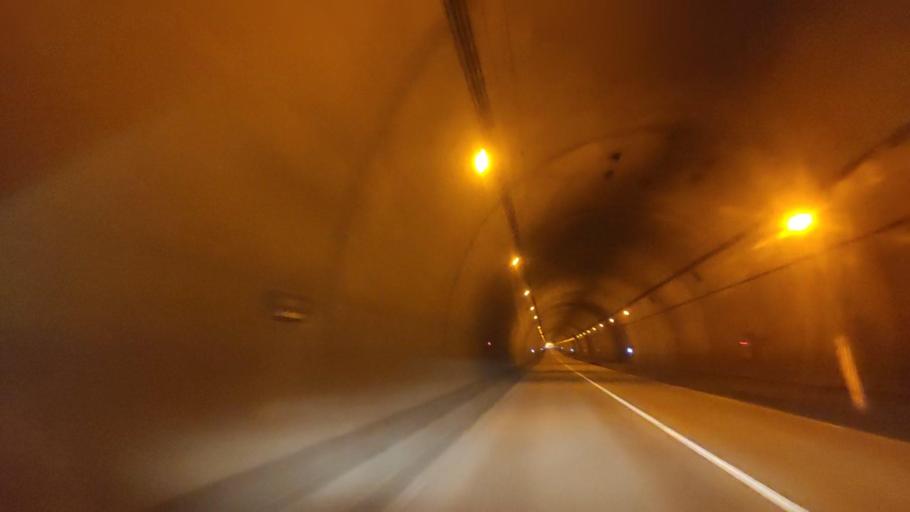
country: JP
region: Hokkaido
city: Date
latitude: 42.5583
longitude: 140.7596
